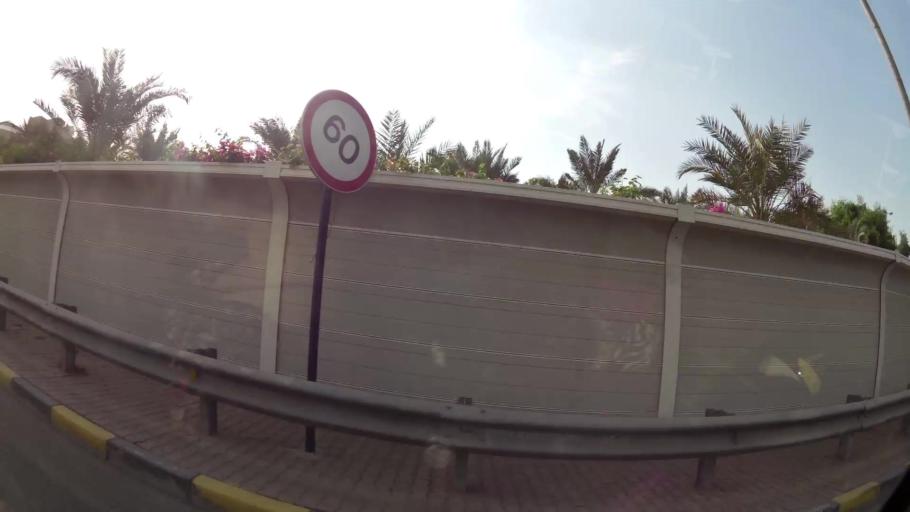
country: KW
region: Al Farwaniyah
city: Al Farwaniyah
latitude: 29.3105
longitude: 47.9768
